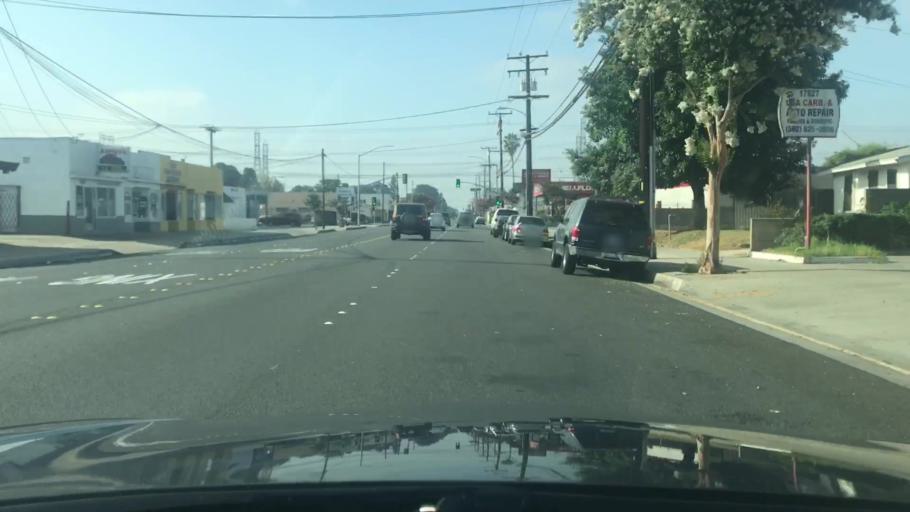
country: US
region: California
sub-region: Los Angeles County
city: Bellflower
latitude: 33.8732
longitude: -118.1340
